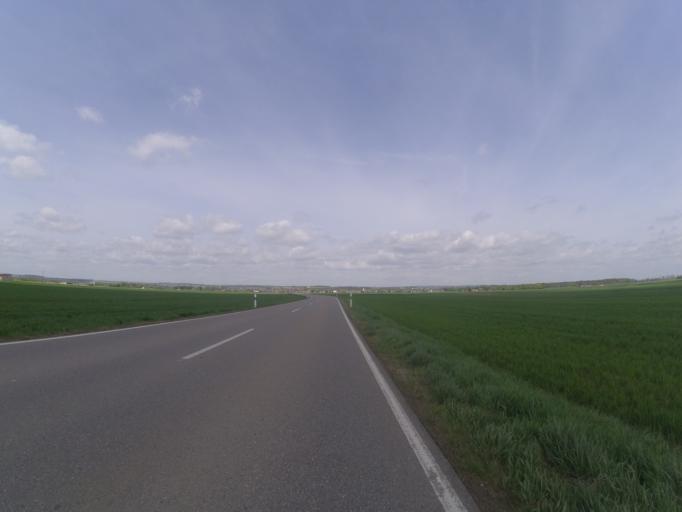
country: DE
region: Baden-Wuerttemberg
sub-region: Tuebingen Region
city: Ersingen
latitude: 48.2792
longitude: 9.8588
